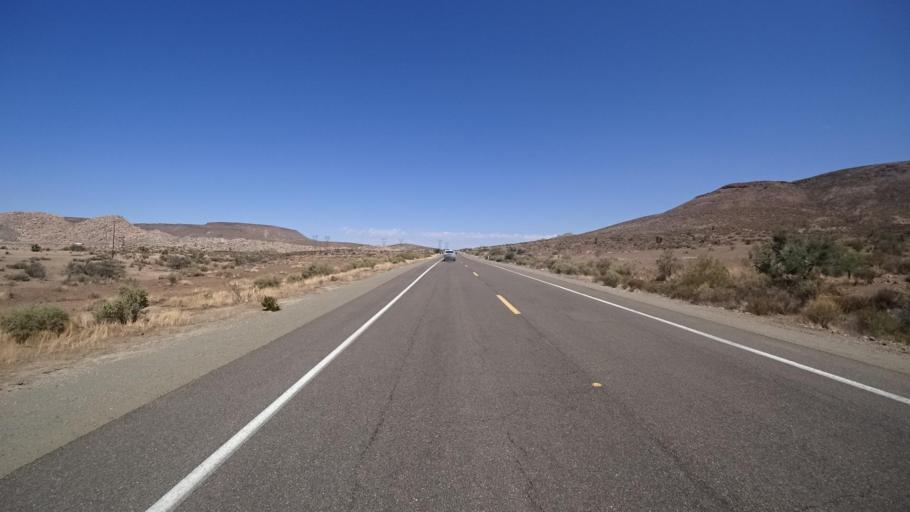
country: MX
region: Baja California
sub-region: Tecate
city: Cereso del Hongo
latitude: 32.6230
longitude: -116.1542
